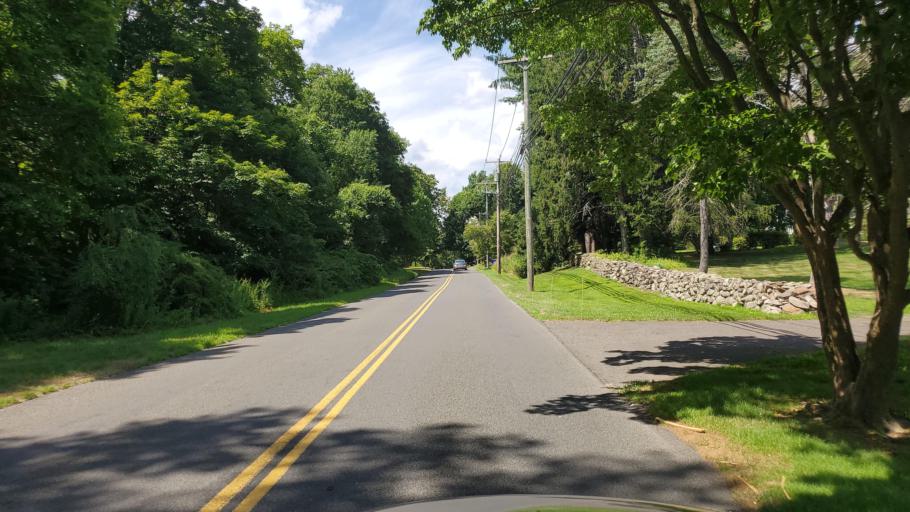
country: US
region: Connecticut
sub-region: Fairfield County
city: Southport
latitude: 41.1872
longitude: -73.3075
